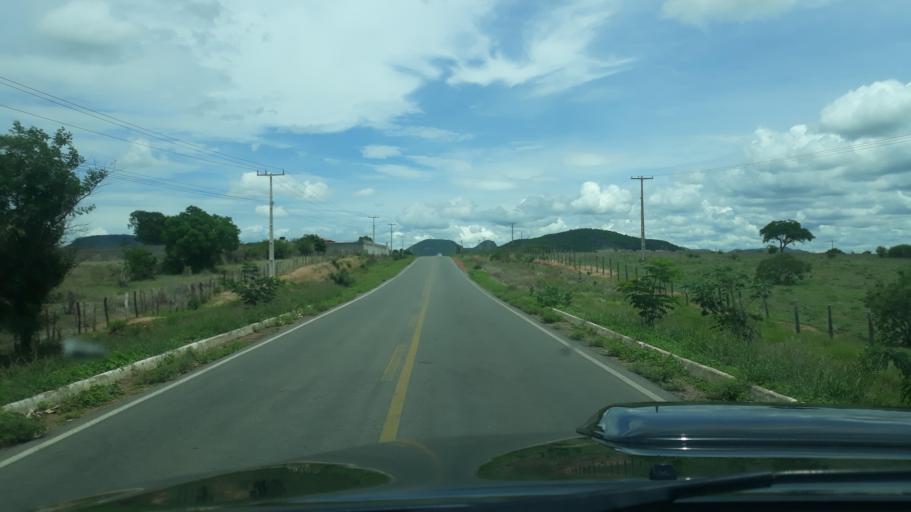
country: BR
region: Bahia
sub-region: Guanambi
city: Guanambi
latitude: -14.2480
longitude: -42.7532
